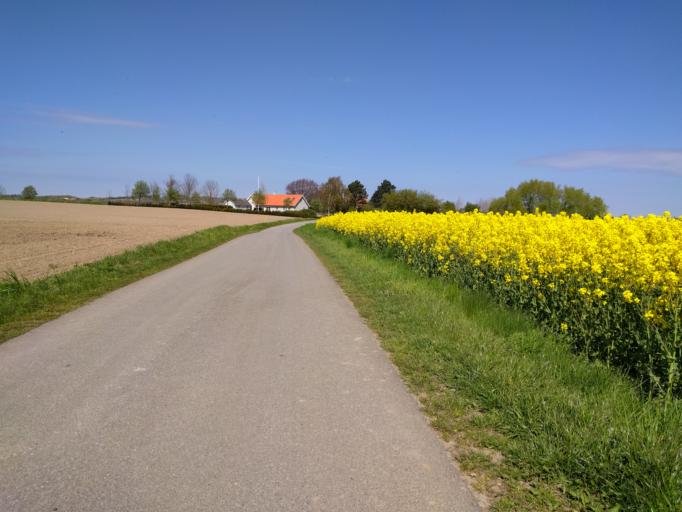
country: DK
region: South Denmark
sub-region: Kerteminde Kommune
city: Munkebo
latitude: 55.4505
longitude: 10.5902
